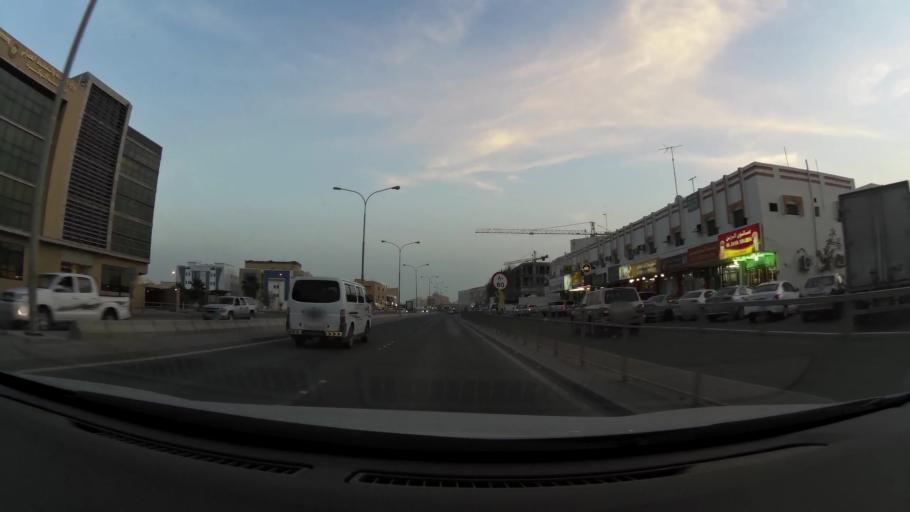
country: QA
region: Al Wakrah
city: Al Wakrah
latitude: 25.1672
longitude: 51.5977
